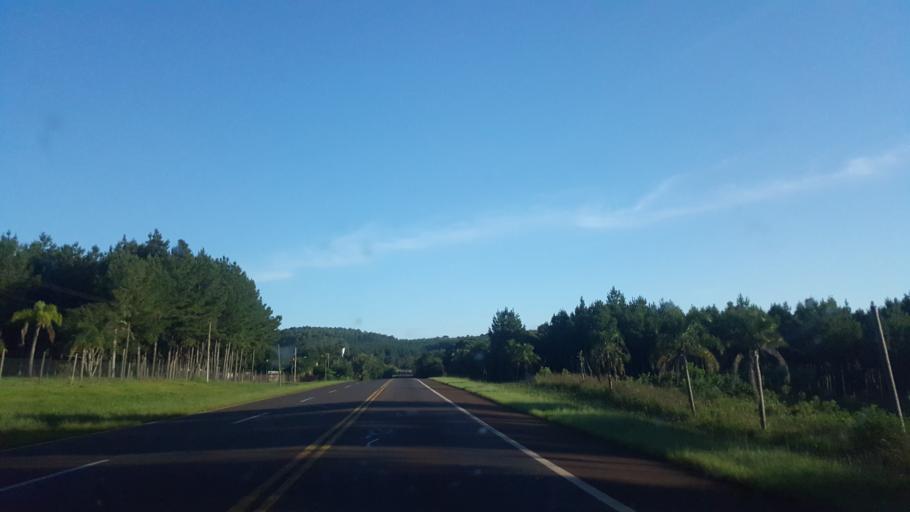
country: AR
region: Misiones
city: Caraguatay
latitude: -26.6535
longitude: -54.7539
